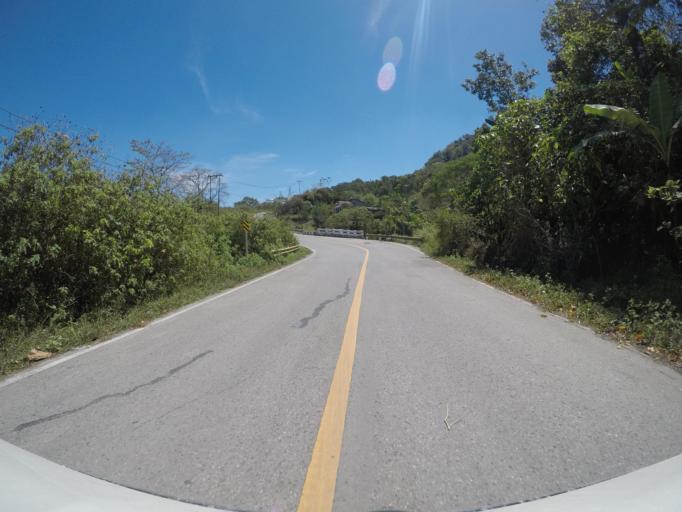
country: TL
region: Manatuto
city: Manatuto
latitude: -8.7888
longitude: 125.9687
